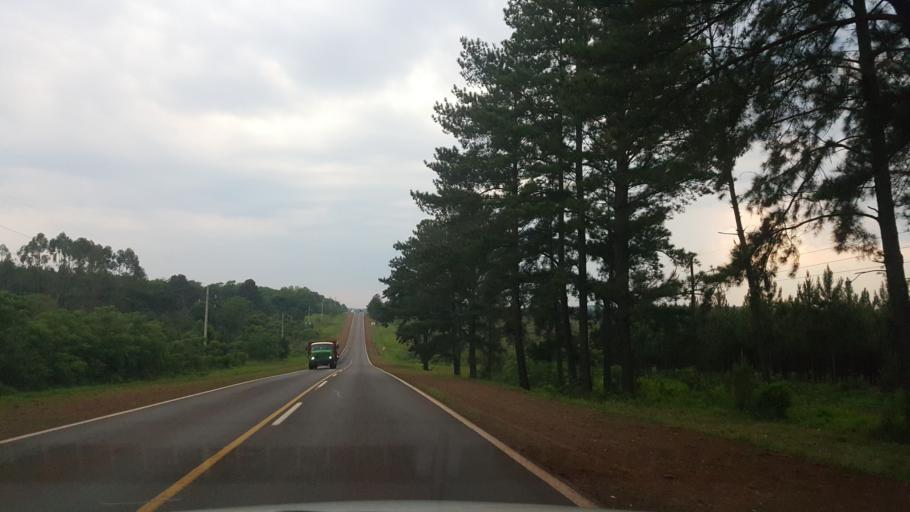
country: AR
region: Misiones
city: Jardin America
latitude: -27.0183
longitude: -55.1966
